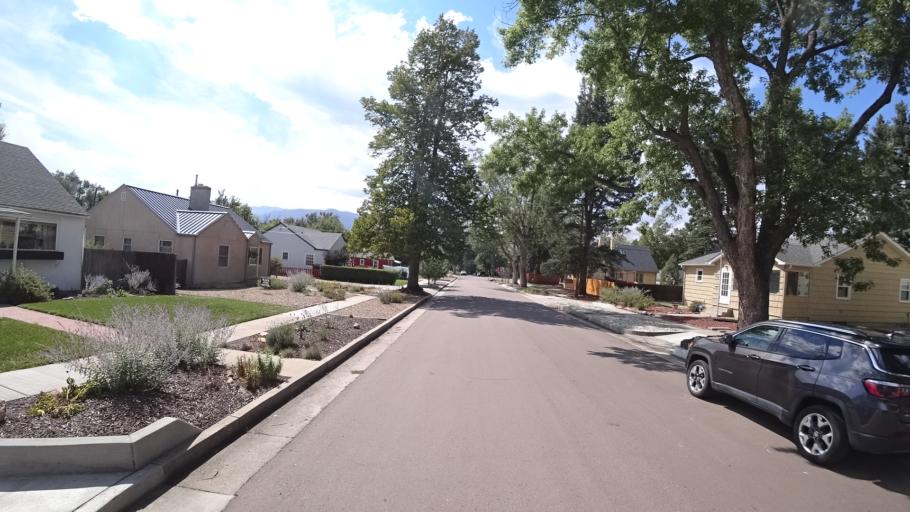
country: US
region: Colorado
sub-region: El Paso County
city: Colorado Springs
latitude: 38.8474
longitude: -104.8065
